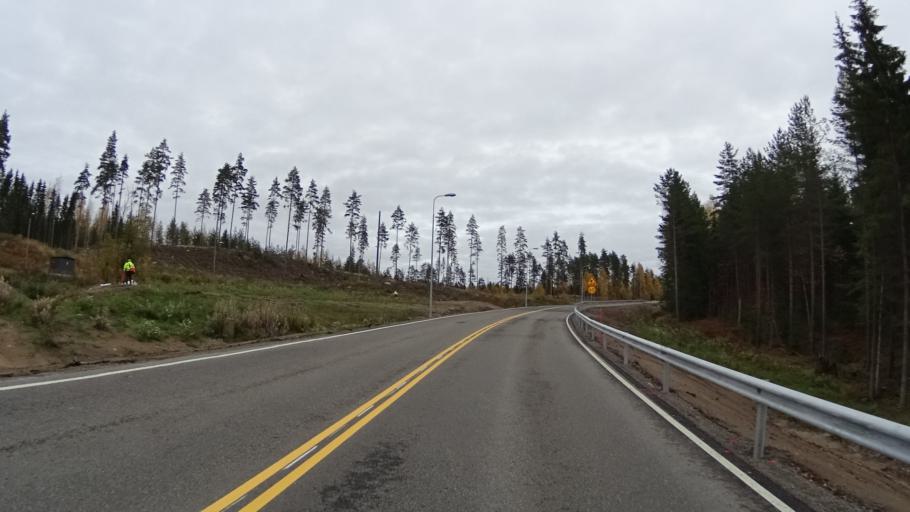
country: FI
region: South Karelia
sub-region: Lappeenranta
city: Luumaeki
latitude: 60.9409
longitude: 27.7054
